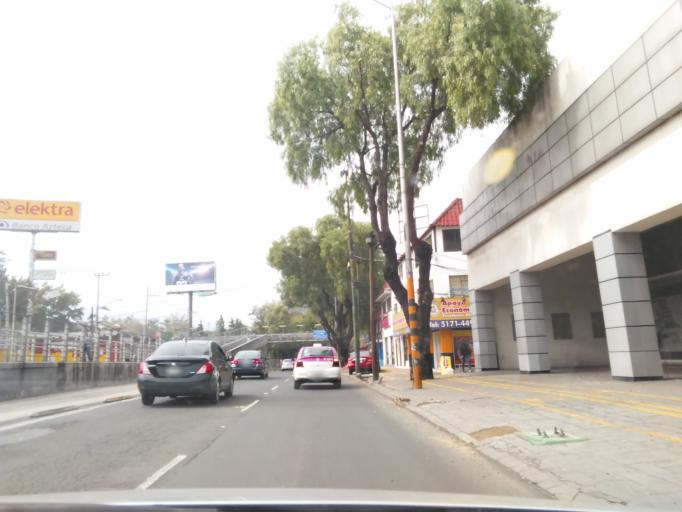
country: MX
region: Mexico City
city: Tlalpan
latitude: 19.2942
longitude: -99.1812
